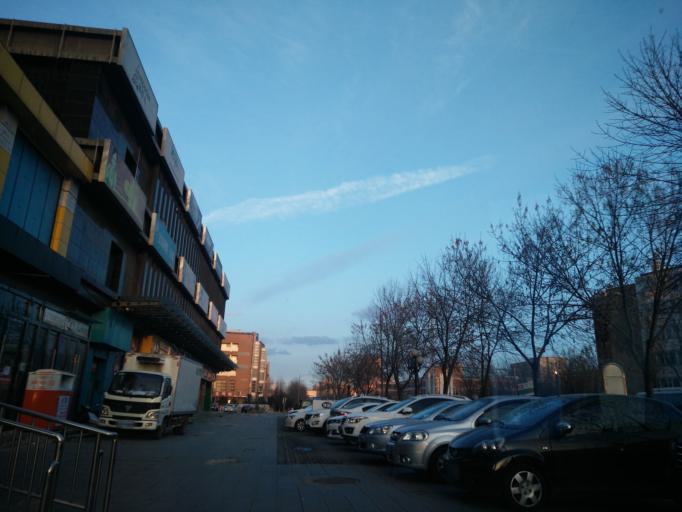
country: CN
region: Beijing
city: Jiugong
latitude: 39.7632
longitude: 116.5042
